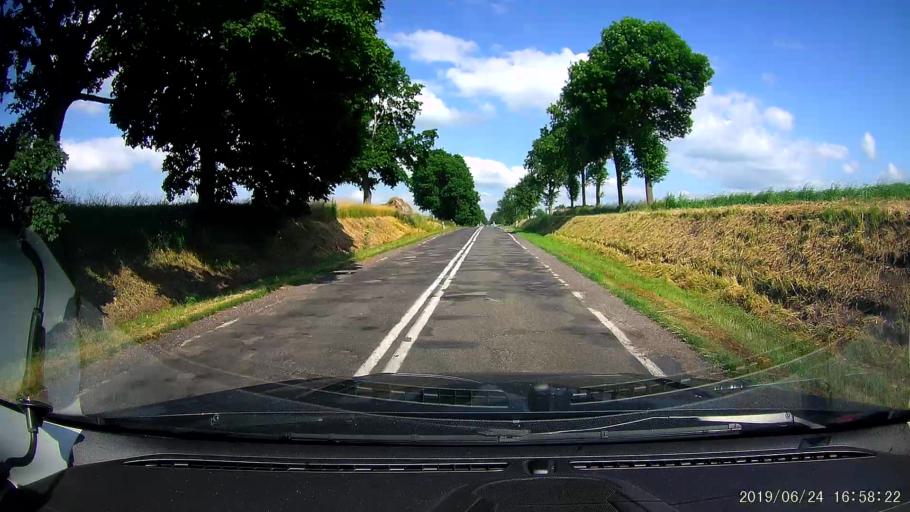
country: PL
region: Lublin Voivodeship
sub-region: Powiat tomaszowski
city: Telatyn
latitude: 50.5253
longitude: 23.8792
